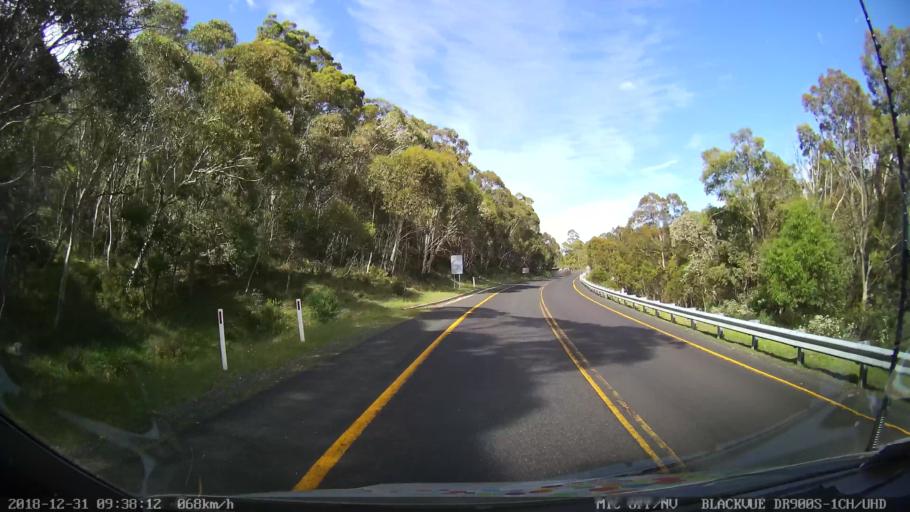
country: AU
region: New South Wales
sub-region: Snowy River
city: Jindabyne
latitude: -36.4729
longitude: 148.3701
